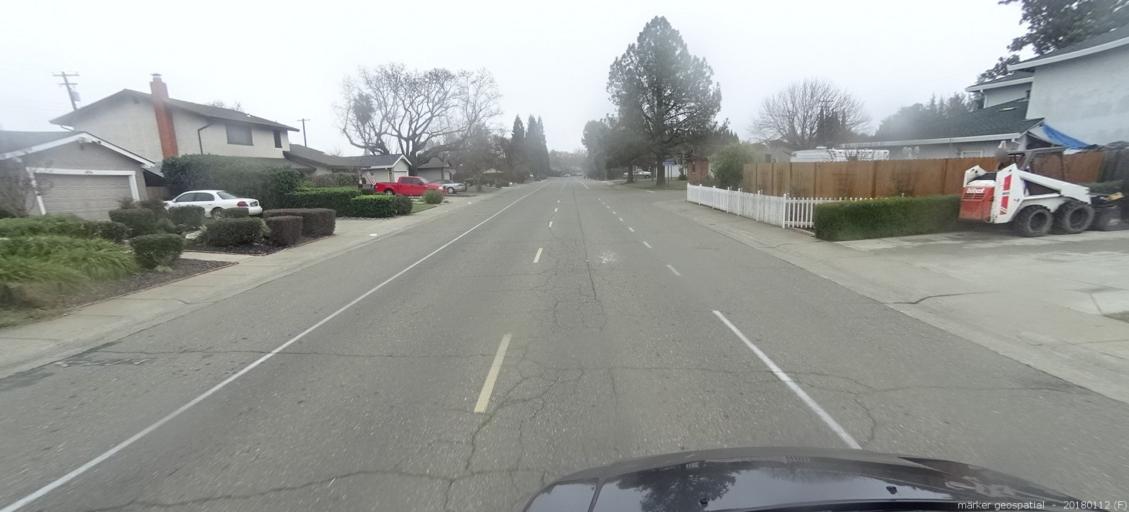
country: US
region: California
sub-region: Sacramento County
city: Rancho Cordova
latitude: 38.6056
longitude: -121.2807
